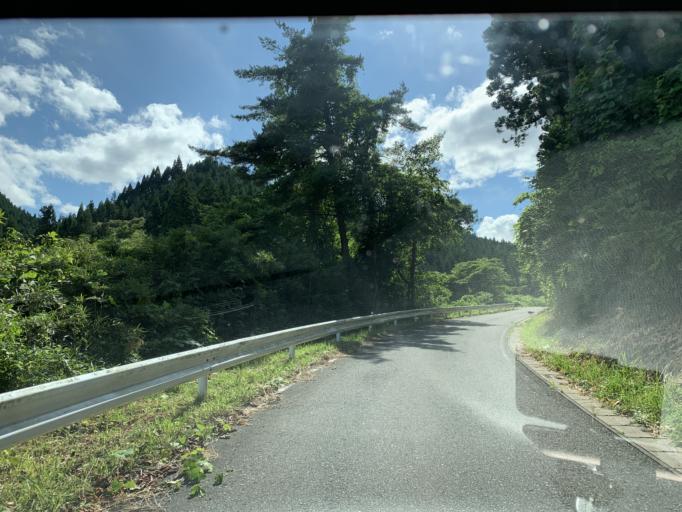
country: JP
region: Iwate
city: Ichinoseki
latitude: 38.9176
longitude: 140.9765
